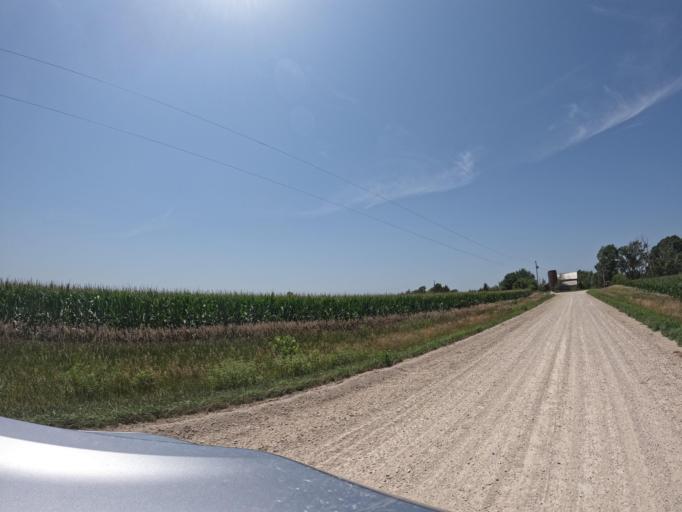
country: US
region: Iowa
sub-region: Henry County
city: Mount Pleasant
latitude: 40.9131
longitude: -91.6446
